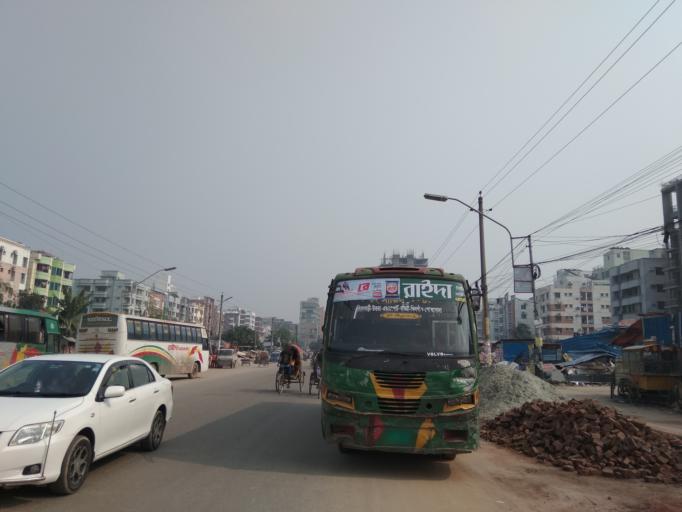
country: BD
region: Dhaka
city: Tungi
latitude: 23.8742
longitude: 90.3860
